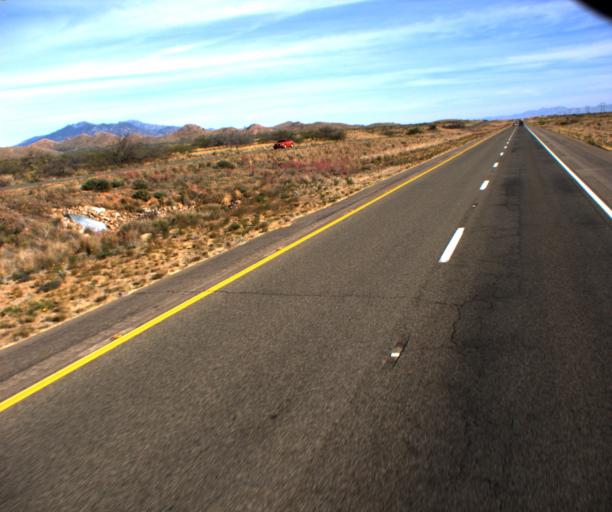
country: US
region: Arizona
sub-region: Graham County
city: Swift Trail Junction
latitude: 32.4780
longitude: -109.6728
